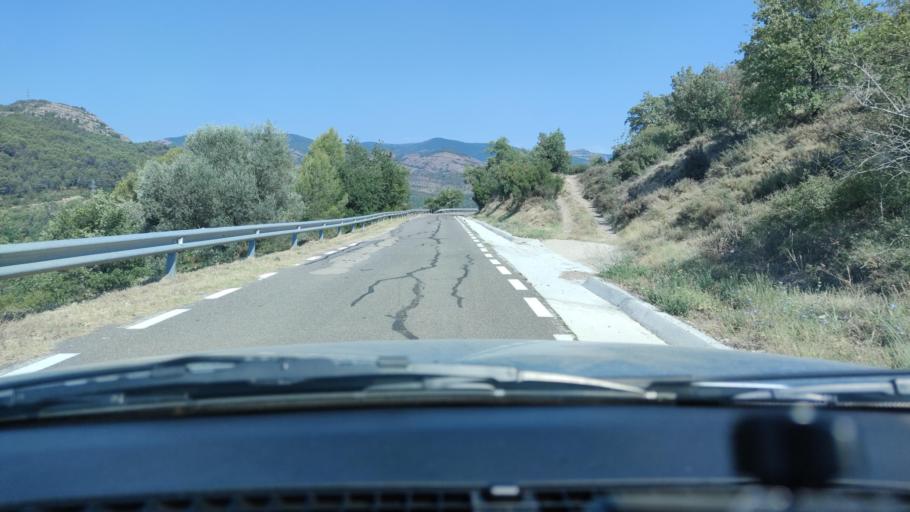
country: ES
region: Catalonia
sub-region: Provincia de Lleida
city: Senterada
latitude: 42.2638
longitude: 0.9540
